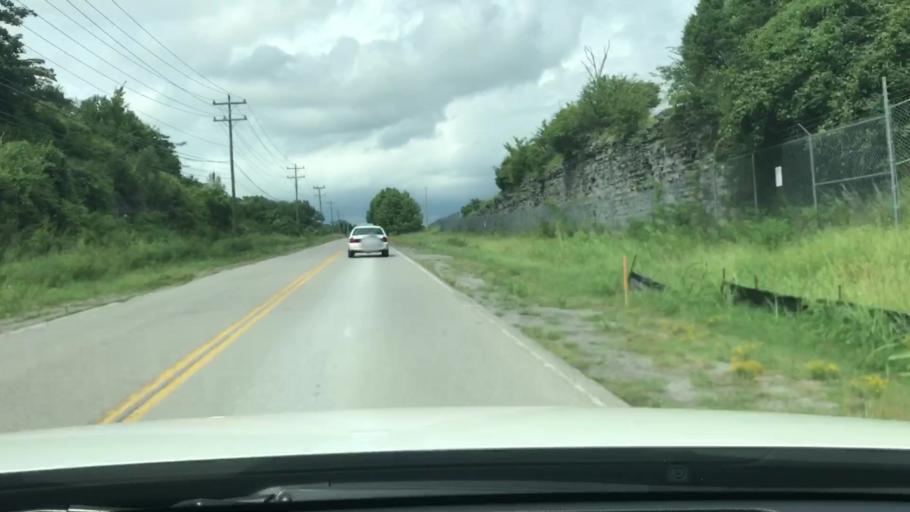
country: US
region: Tennessee
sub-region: Davidson County
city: Oak Hill
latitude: 36.0998
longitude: -86.6924
